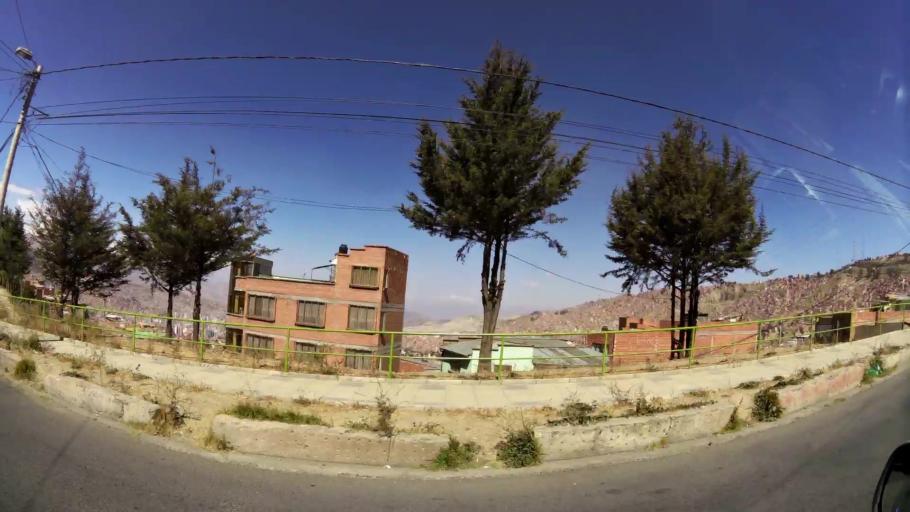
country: BO
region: La Paz
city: La Paz
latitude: -16.4859
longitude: -68.1594
